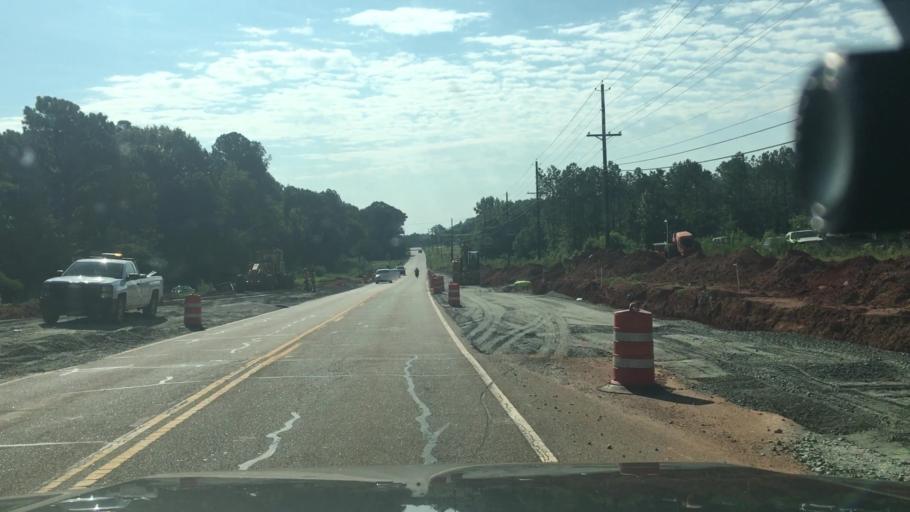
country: US
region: Georgia
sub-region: Coweta County
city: East Newnan
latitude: 33.3589
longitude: -84.7513
